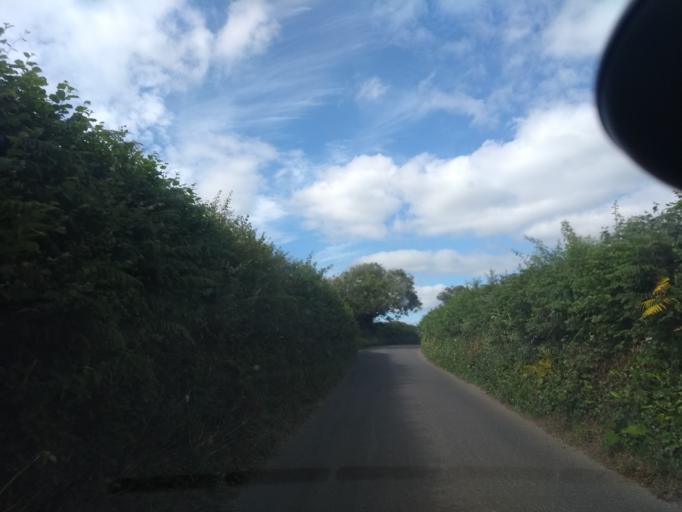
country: GB
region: England
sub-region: Devon
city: Modbury
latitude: 50.3011
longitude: -3.8886
